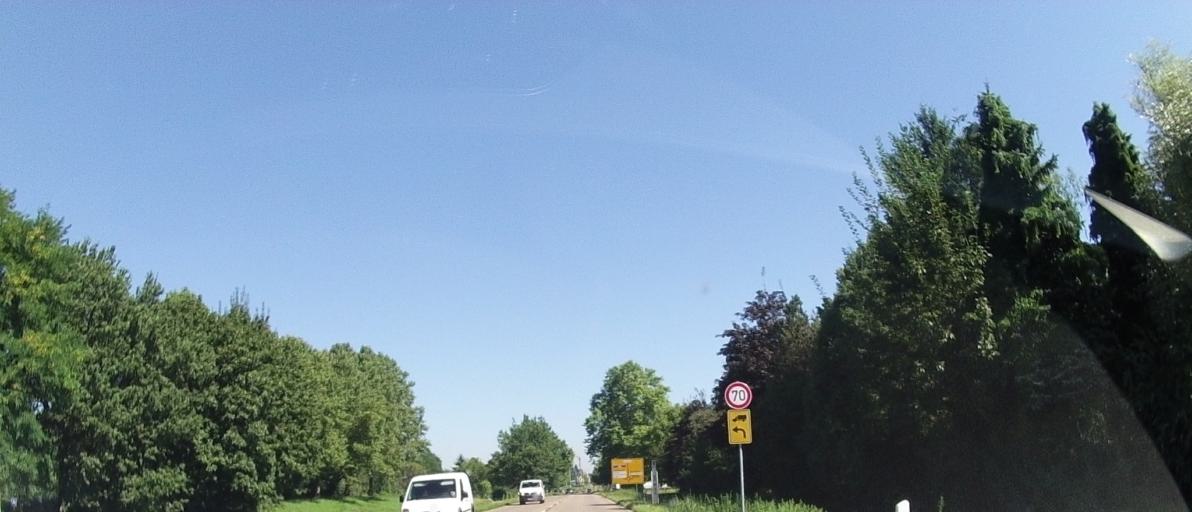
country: DE
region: Baden-Wuerttemberg
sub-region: Karlsruhe Region
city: Buhl
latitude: 48.6876
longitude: 8.1304
